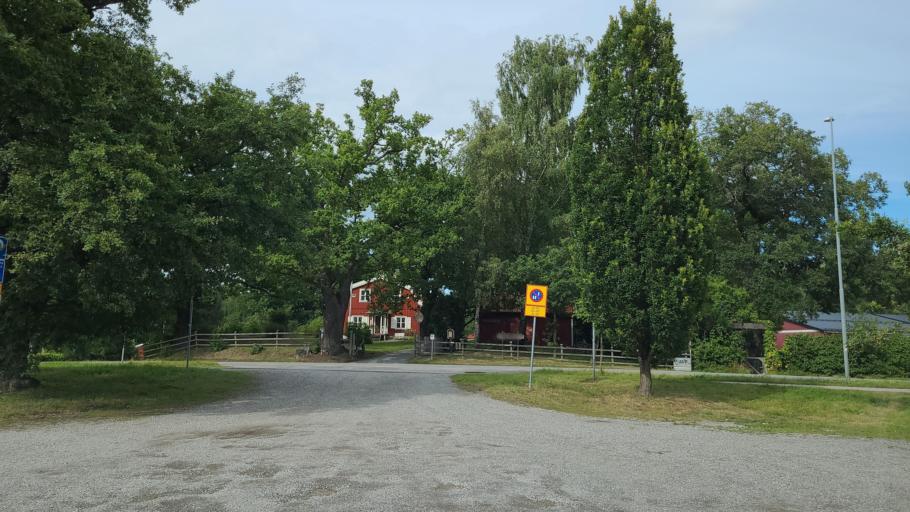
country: SE
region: Stockholm
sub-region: Jarfalla Kommun
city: Jakobsberg
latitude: 59.4567
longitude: 17.8224
